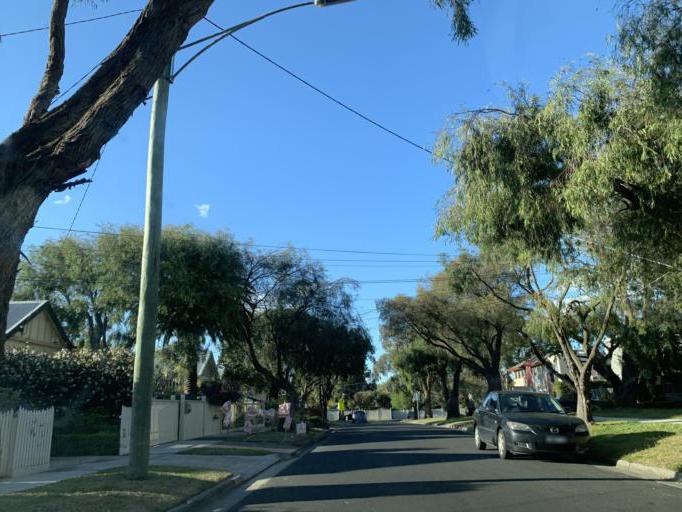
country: AU
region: Victoria
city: Hampton
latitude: -37.9462
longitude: 145.0085
